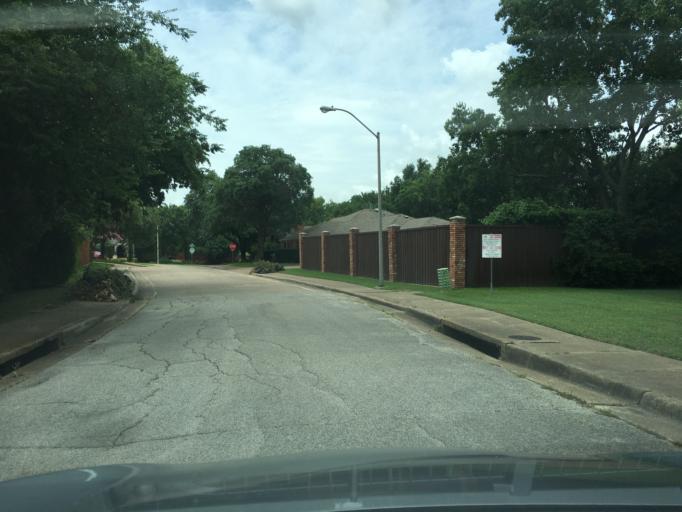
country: US
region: Texas
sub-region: Dallas County
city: Richardson
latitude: 32.9134
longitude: -96.7150
